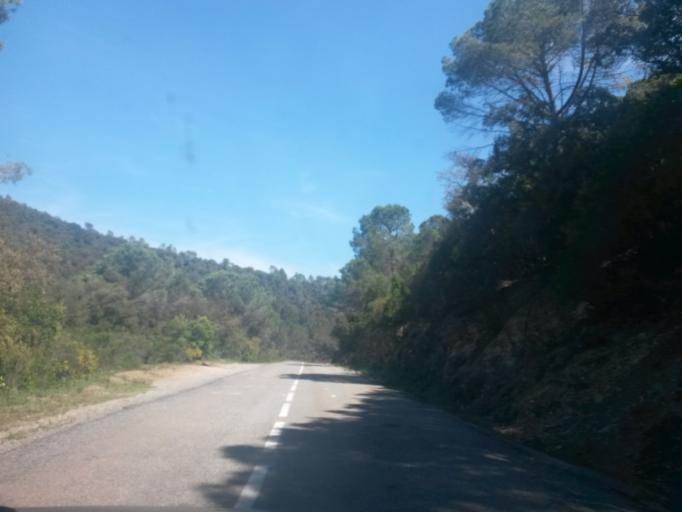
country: ES
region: Catalonia
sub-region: Provincia de Girona
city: Madremanya
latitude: 41.9817
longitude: 2.9404
